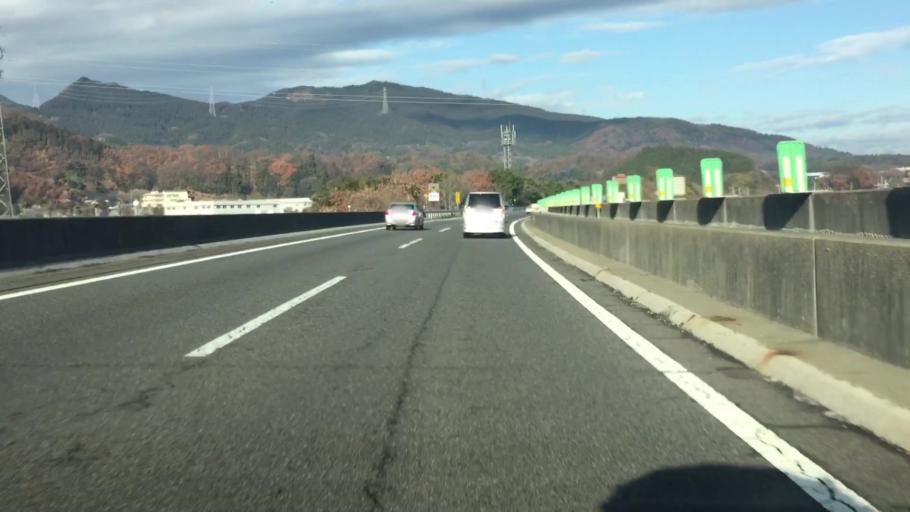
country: JP
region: Gunma
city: Tomioka
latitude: 36.2376
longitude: 138.8197
